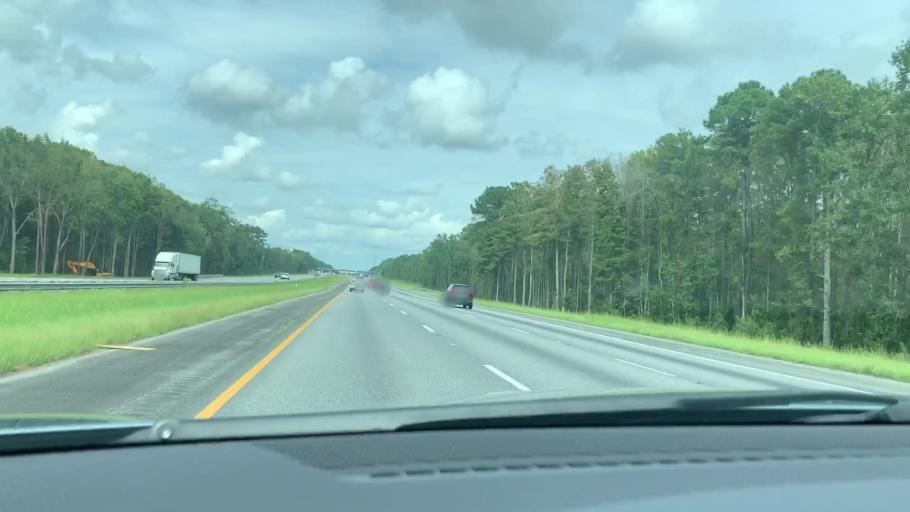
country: US
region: Georgia
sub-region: Liberty County
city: Midway
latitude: 31.6257
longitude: -81.4082
